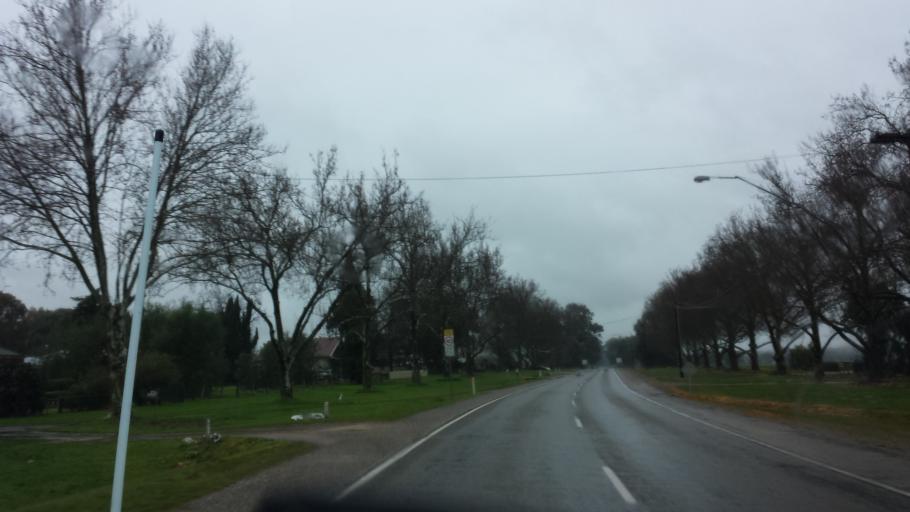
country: AU
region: Victoria
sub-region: Wangaratta
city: Wangaratta
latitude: -36.4341
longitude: 146.5434
